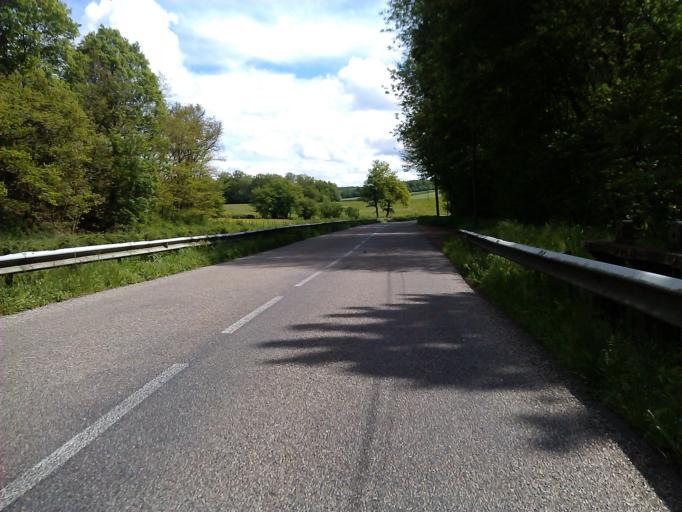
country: FR
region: Bourgogne
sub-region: Departement de Saone-et-Loire
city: Ecuisses
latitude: 46.7891
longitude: 4.5574
